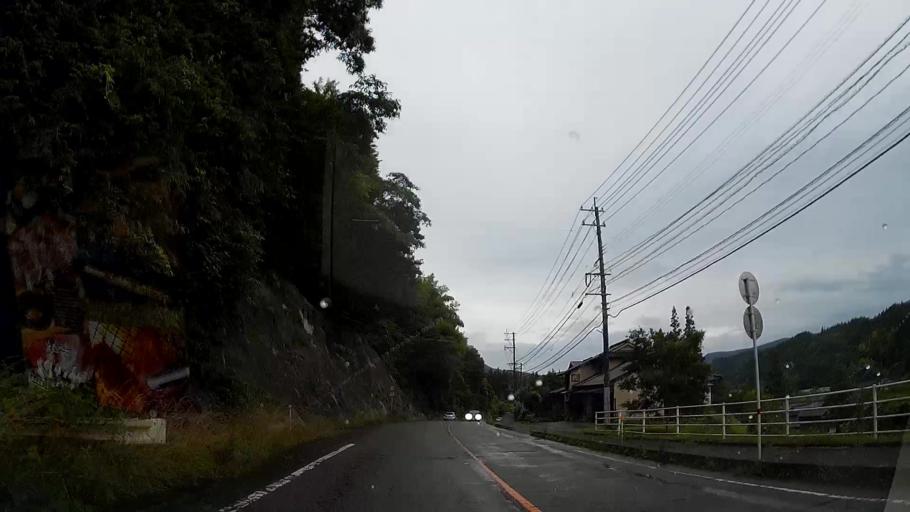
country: JP
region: Oita
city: Tsukawaki
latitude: 33.1467
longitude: 131.0556
